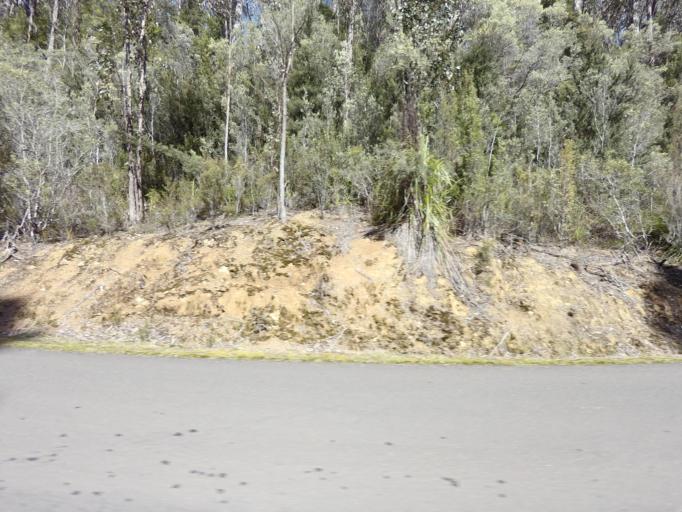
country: AU
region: Tasmania
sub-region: Derwent Valley
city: New Norfolk
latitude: -42.7511
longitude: 146.5072
